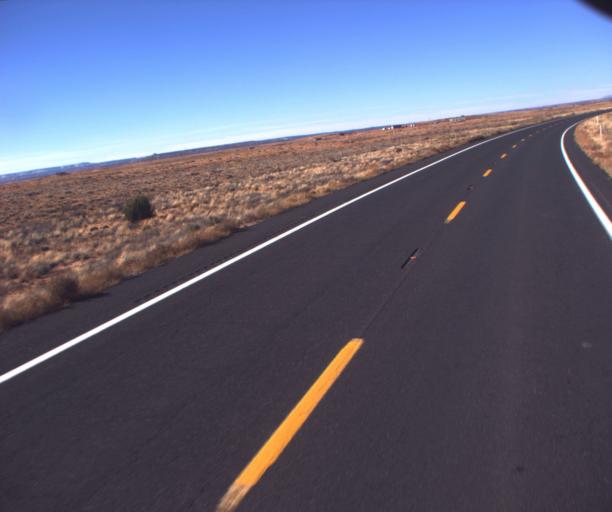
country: US
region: Arizona
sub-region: Coconino County
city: Kaibito
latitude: 36.4833
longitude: -110.7045
